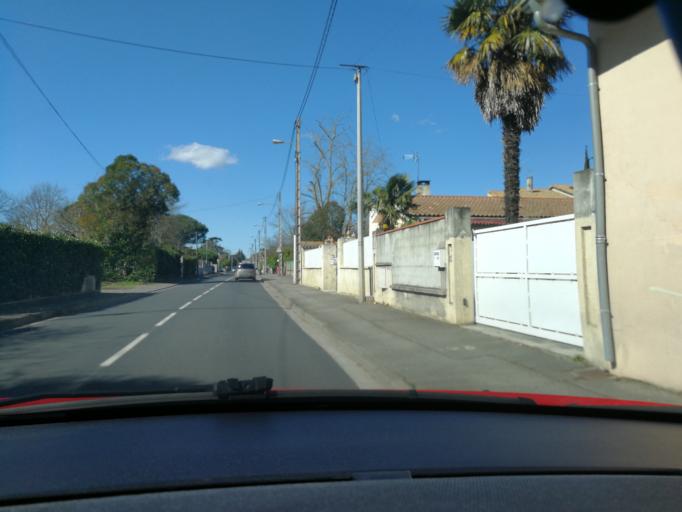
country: FR
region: Midi-Pyrenees
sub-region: Departement de la Haute-Garonne
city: Cugnaux
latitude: 43.5519
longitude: 1.3777
